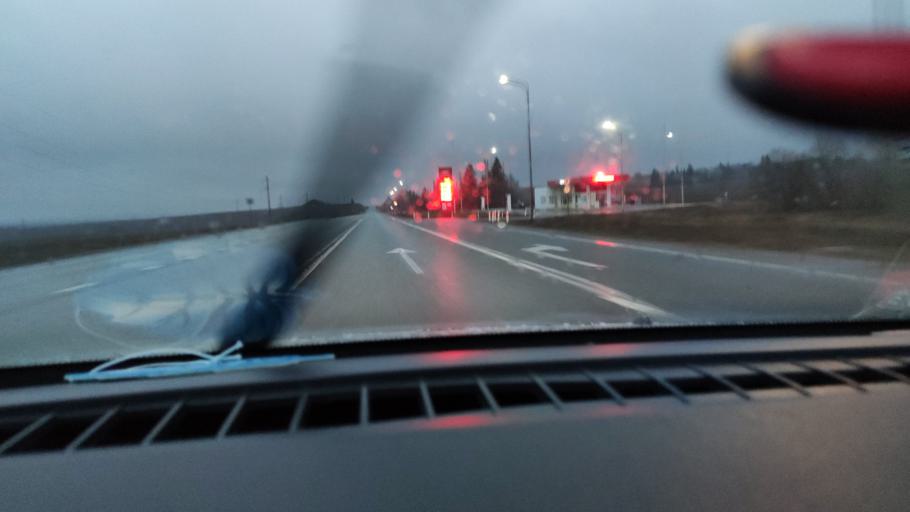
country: RU
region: Udmurtiya
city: Alnashi
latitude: 56.2501
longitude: 52.3843
